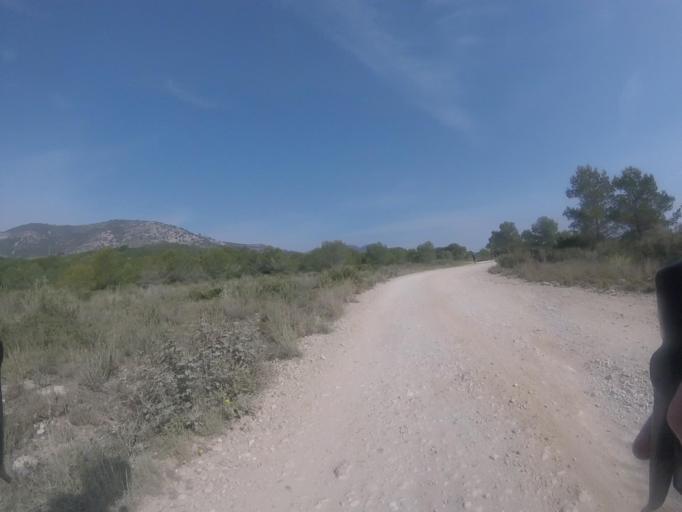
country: ES
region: Valencia
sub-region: Provincia de Castello
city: Alcoceber
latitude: 40.2756
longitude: 0.3117
